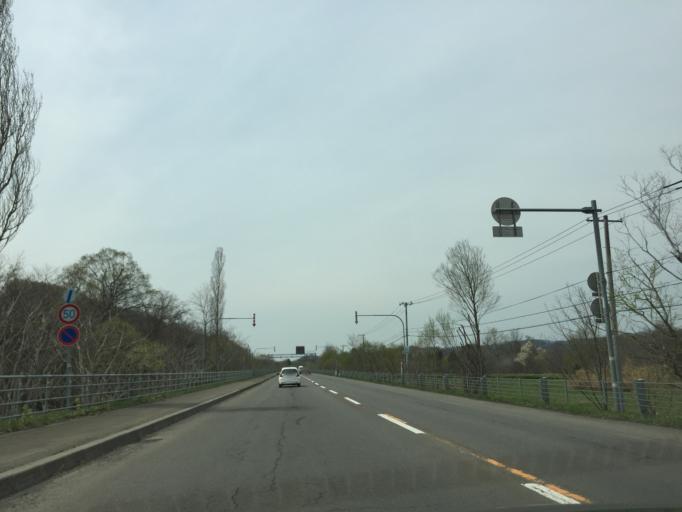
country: JP
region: Hokkaido
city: Ashibetsu
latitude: 43.5327
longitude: 142.1660
